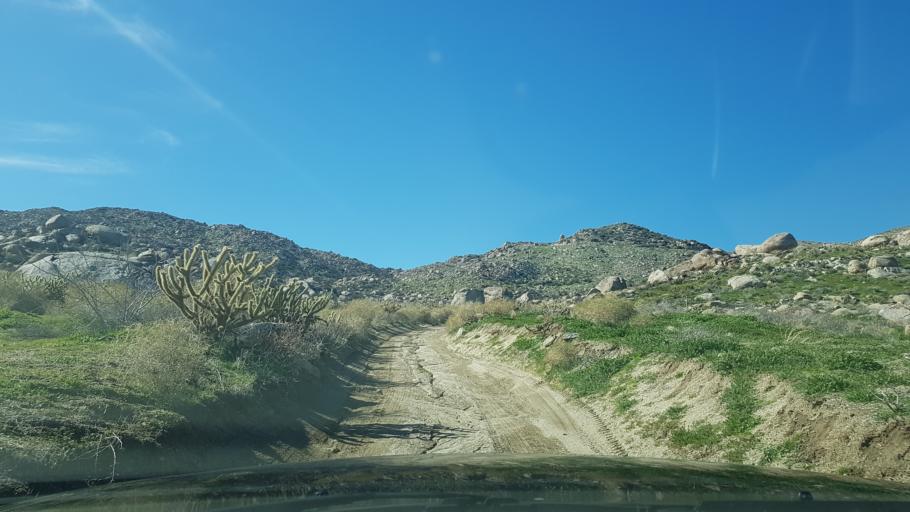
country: US
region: California
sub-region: San Diego County
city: Borrego Springs
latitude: 33.2109
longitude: -116.4581
